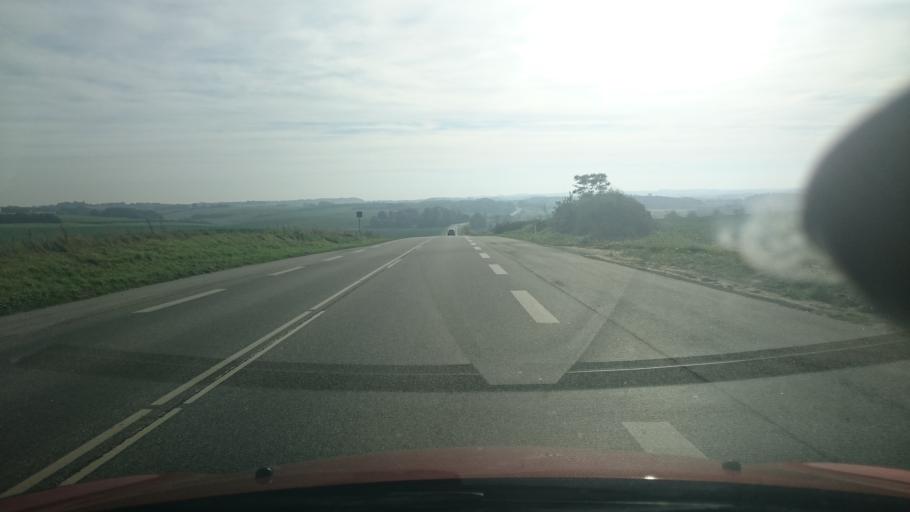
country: DK
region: Central Jutland
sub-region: Syddjurs Kommune
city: Hornslet
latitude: 56.3755
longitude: 10.3088
